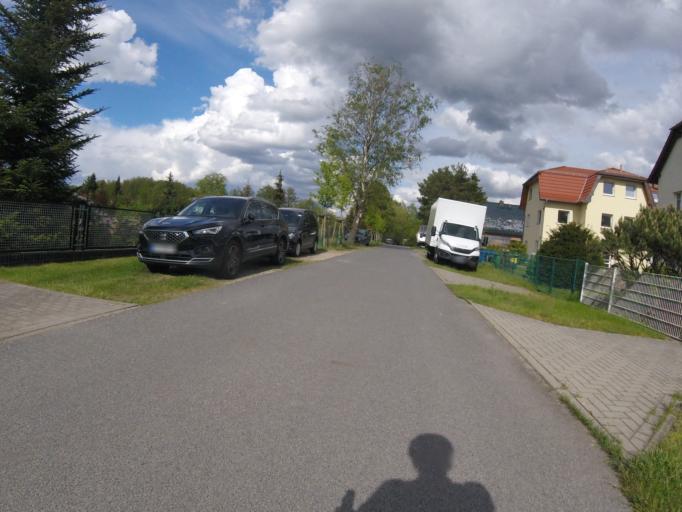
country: DE
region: Brandenburg
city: Bestensee
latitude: 52.2349
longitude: 13.6196
